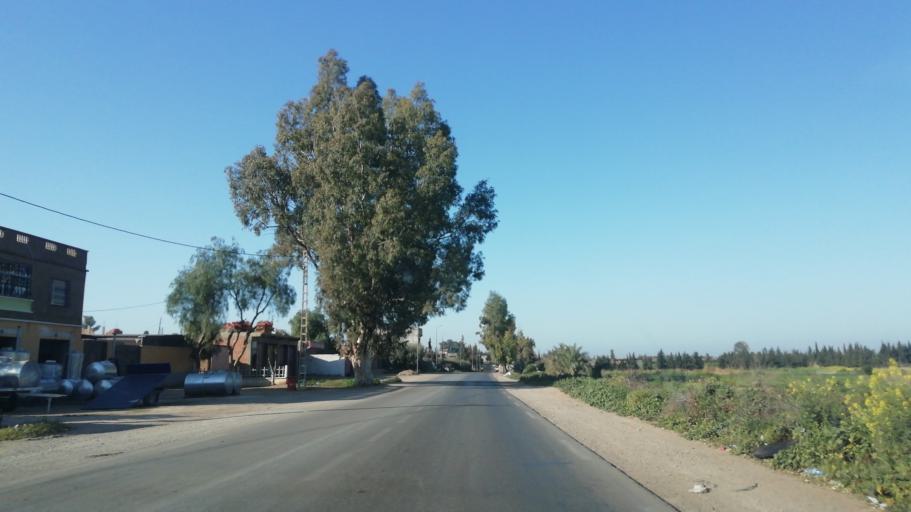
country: DZ
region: Mascara
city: Mascara
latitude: 35.6272
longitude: 0.1253
